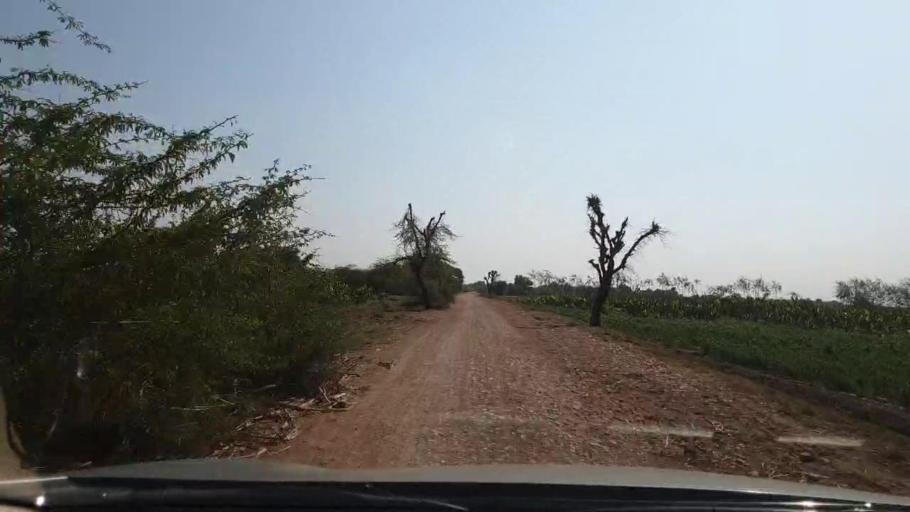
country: PK
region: Sindh
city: Mirpur Khas
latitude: 25.5957
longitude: 68.8673
